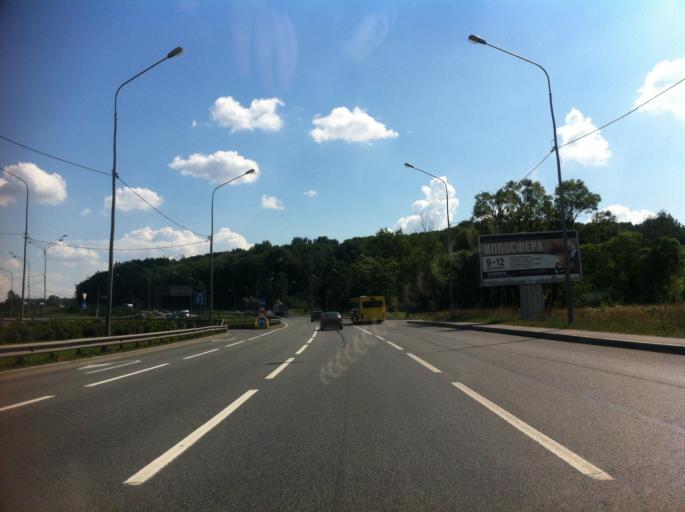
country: RU
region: St.-Petersburg
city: Aleksandrovskaya
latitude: 59.7779
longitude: 30.3251
